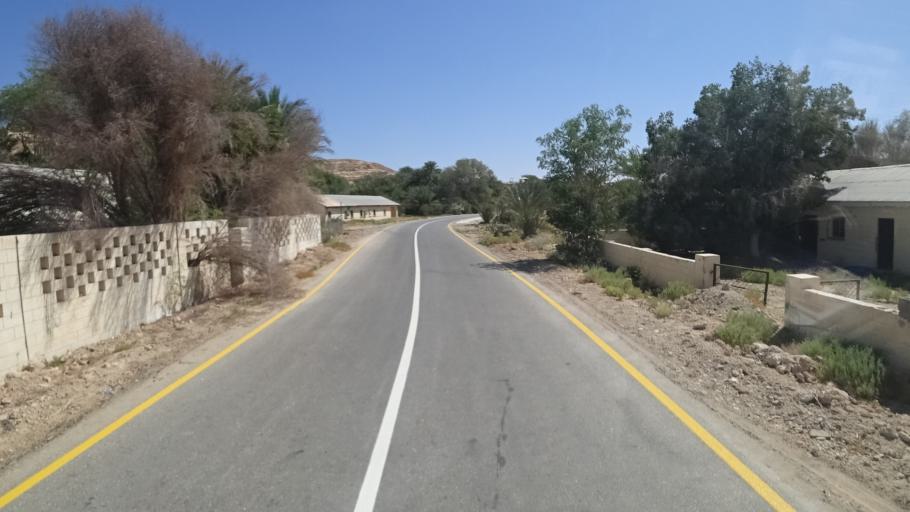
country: OM
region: Zufar
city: Salalah
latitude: 17.4790
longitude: 53.3519
